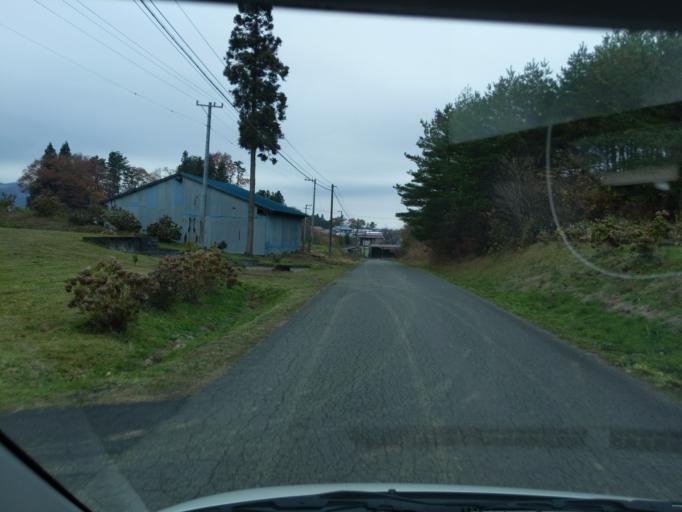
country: JP
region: Iwate
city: Ichinoseki
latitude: 38.9970
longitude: 141.0254
